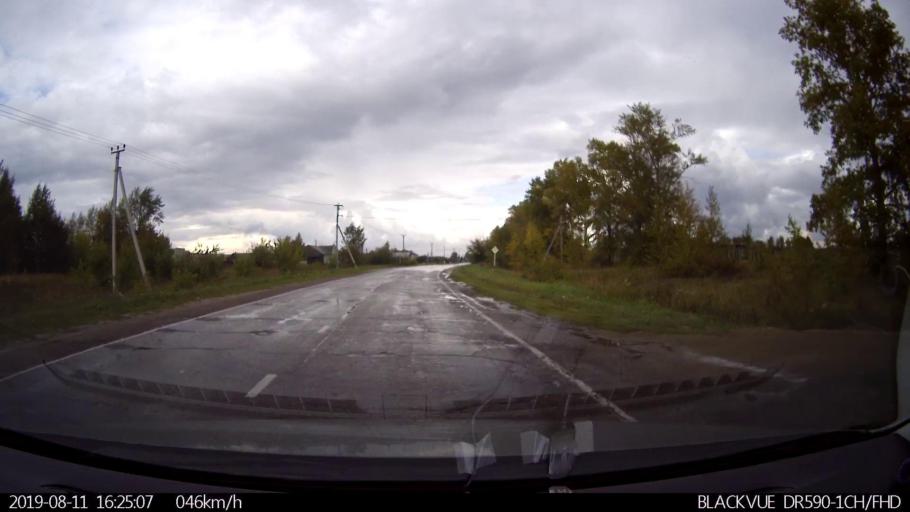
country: RU
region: Ulyanovsk
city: Mayna
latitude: 54.1043
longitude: 47.6011
